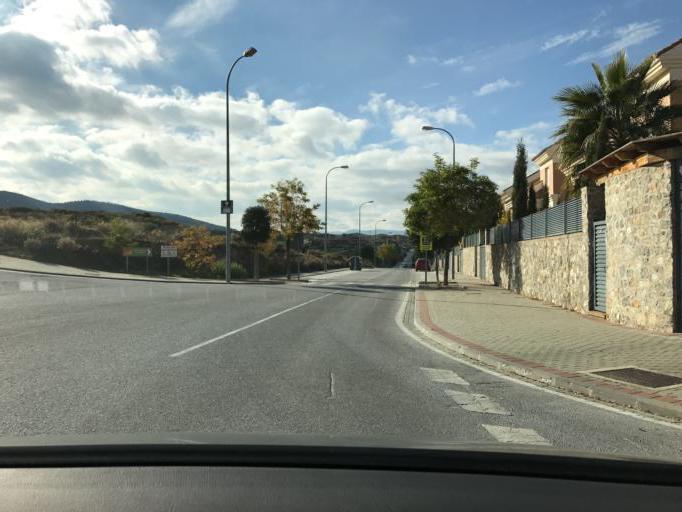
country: ES
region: Andalusia
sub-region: Provincia de Granada
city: Otura
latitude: 37.0786
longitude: -3.6320
